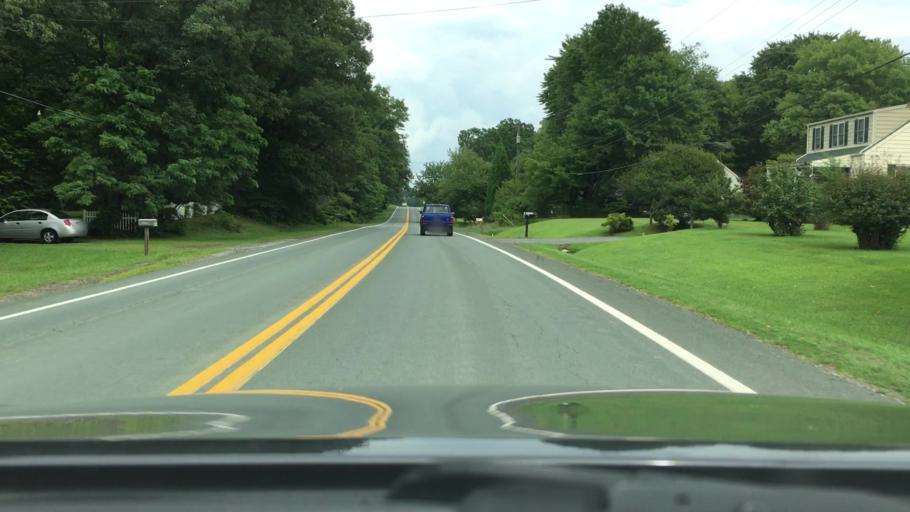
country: US
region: Virginia
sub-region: Orange County
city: Orange
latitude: 38.2554
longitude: -78.0209
